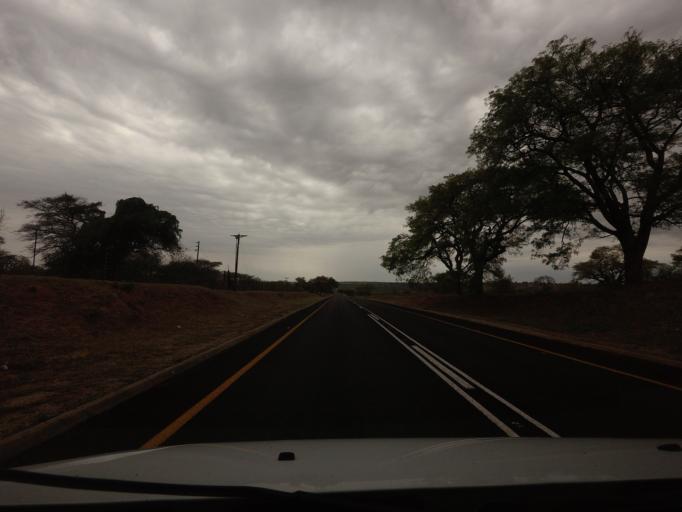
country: ZA
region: Limpopo
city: Thulamahashi
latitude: -24.5659
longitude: 31.1113
